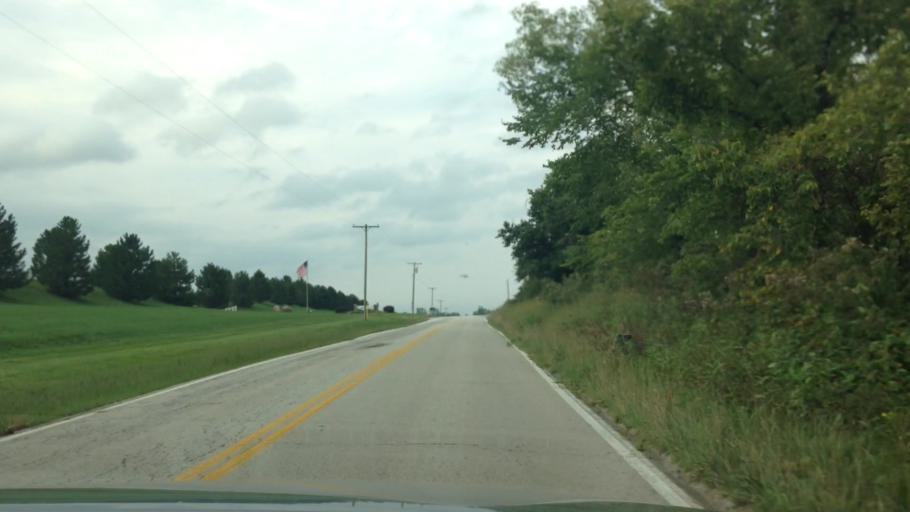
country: US
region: Missouri
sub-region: Platte County
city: Platte City
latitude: 39.3455
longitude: -94.6801
